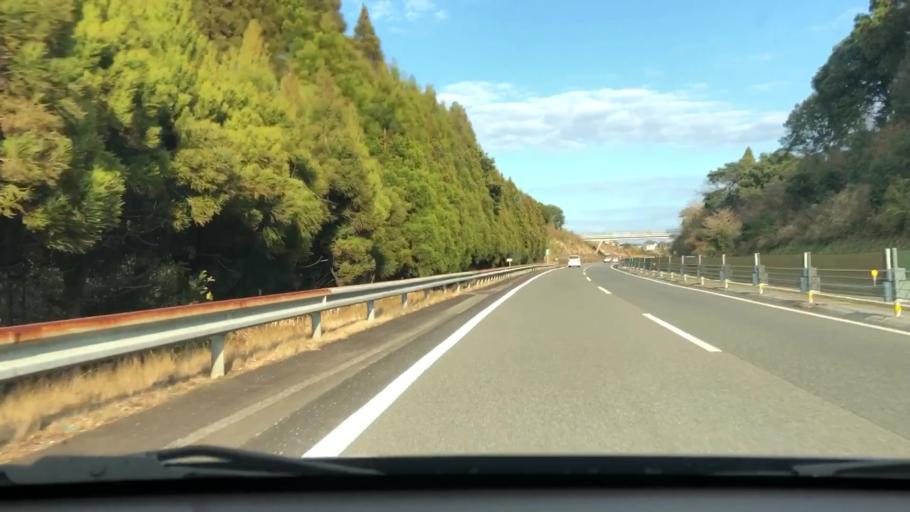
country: JP
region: Miyazaki
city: Miyazaki-shi
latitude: 31.8304
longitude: 131.3153
